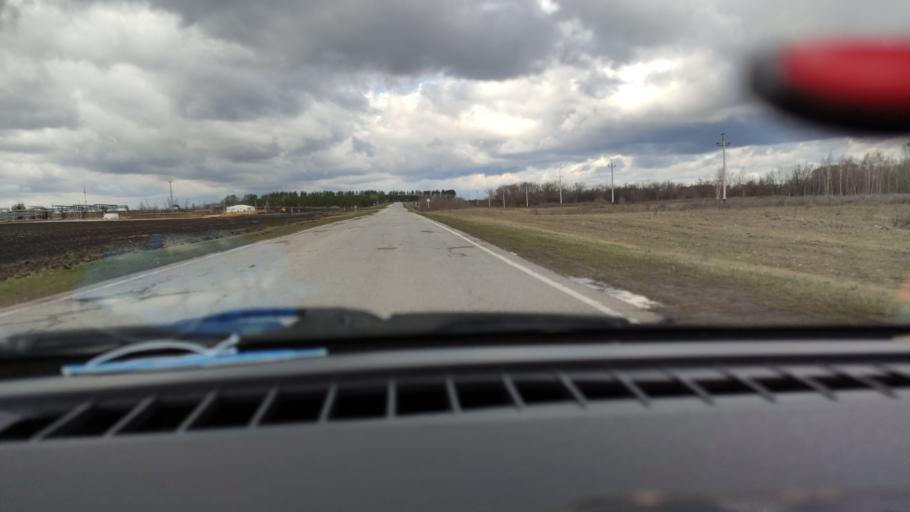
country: RU
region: Samara
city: Novyy Buyan
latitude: 53.7700
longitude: 49.9618
